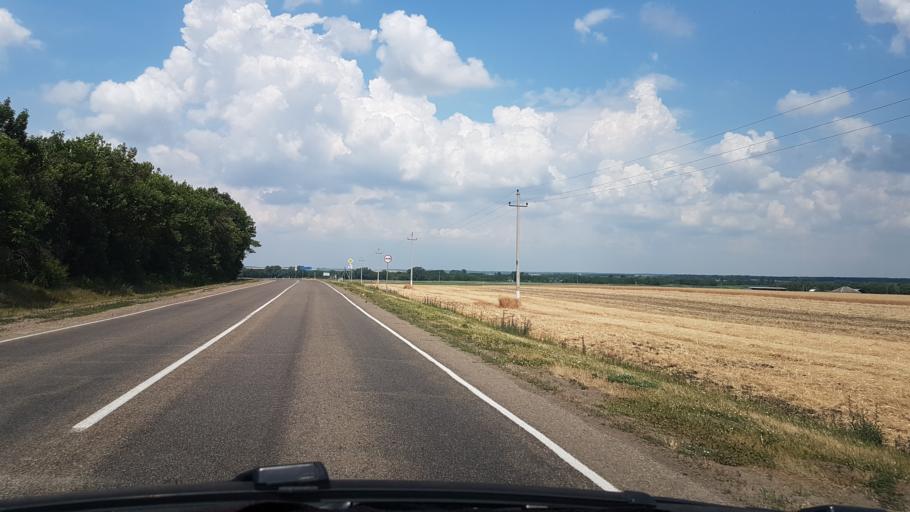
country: RU
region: Krasnodarskiy
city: Dmitriyevskaya
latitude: 45.6959
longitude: 40.7442
